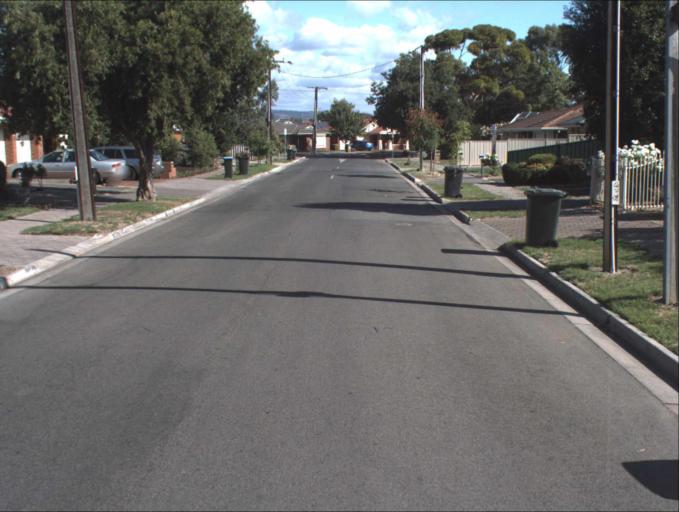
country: AU
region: South Australia
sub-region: Port Adelaide Enfield
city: Gilles Plains
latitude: -34.8631
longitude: 138.6450
